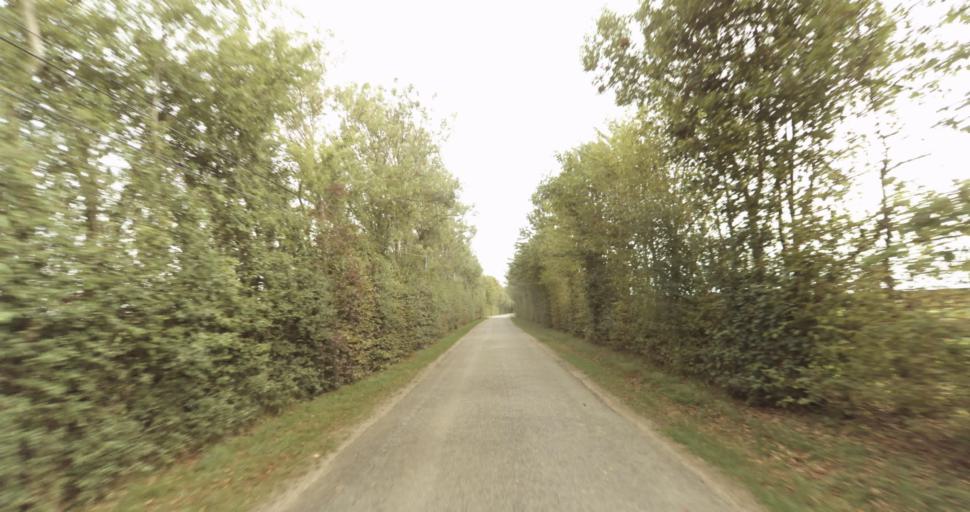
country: FR
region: Lower Normandy
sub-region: Departement de l'Orne
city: Sainte-Gauburge-Sainte-Colombe
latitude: 48.7366
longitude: 0.3653
